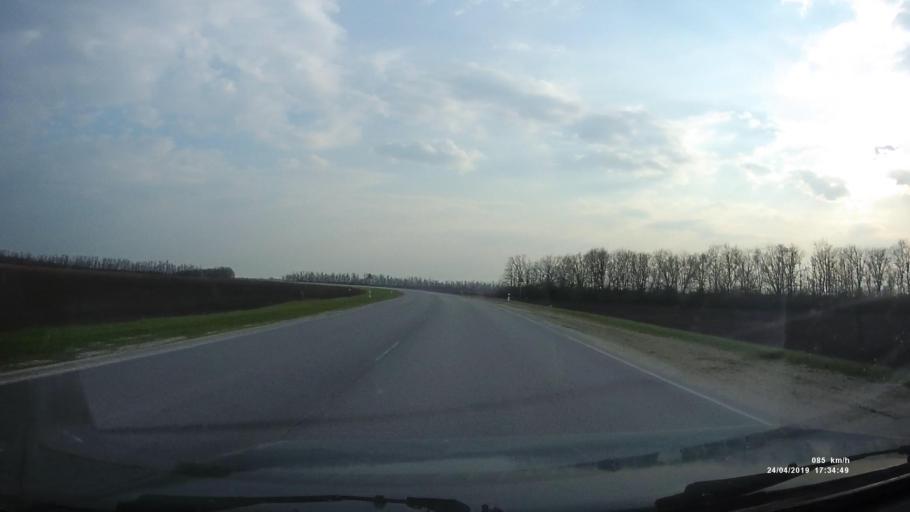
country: RU
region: Rostov
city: Tselina
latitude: 46.5241
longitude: 41.0754
